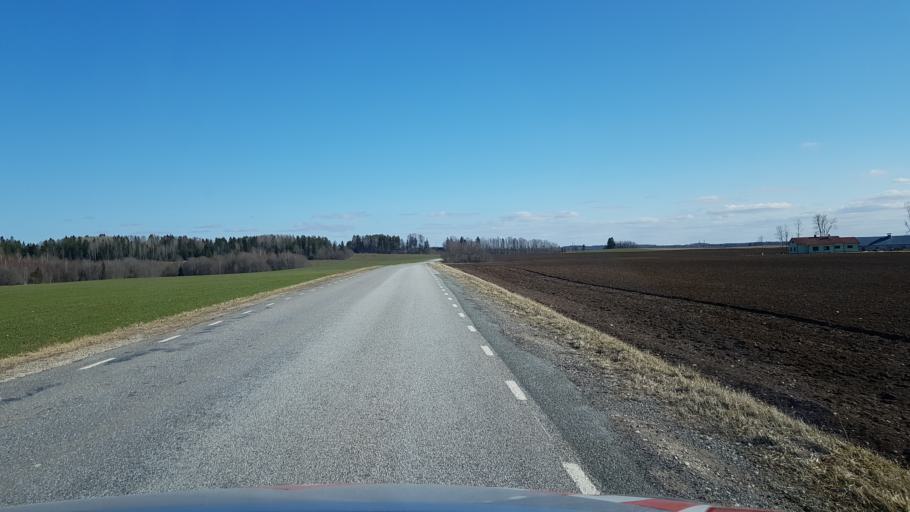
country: EE
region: Laeaene-Virumaa
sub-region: Kadrina vald
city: Kadrina
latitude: 59.3584
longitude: 26.0637
